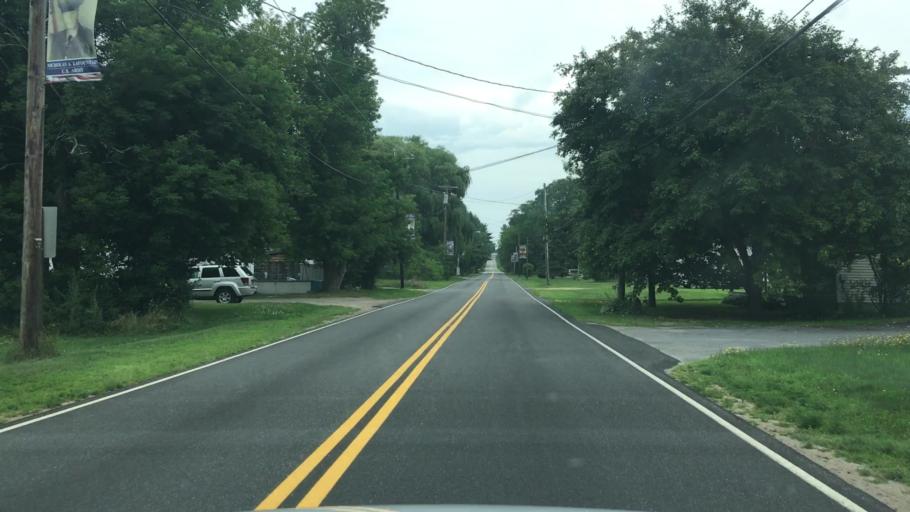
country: US
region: New York
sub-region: Essex County
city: Keeseville
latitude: 44.5016
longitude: -73.4736
